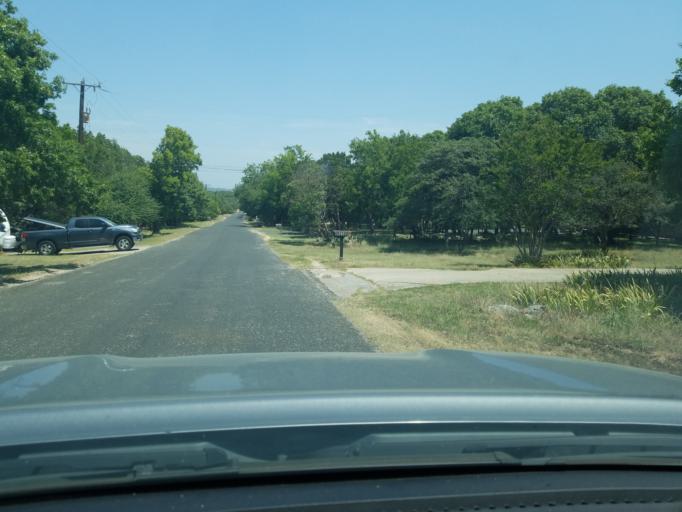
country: US
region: Texas
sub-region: Bexar County
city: Timberwood Park
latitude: 29.7148
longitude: -98.4924
